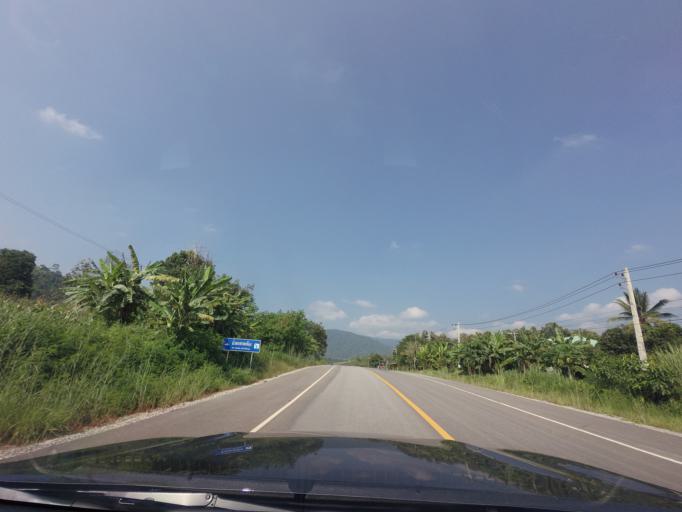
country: TH
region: Loei
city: Na Haeo
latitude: 17.4977
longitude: 101.0179
